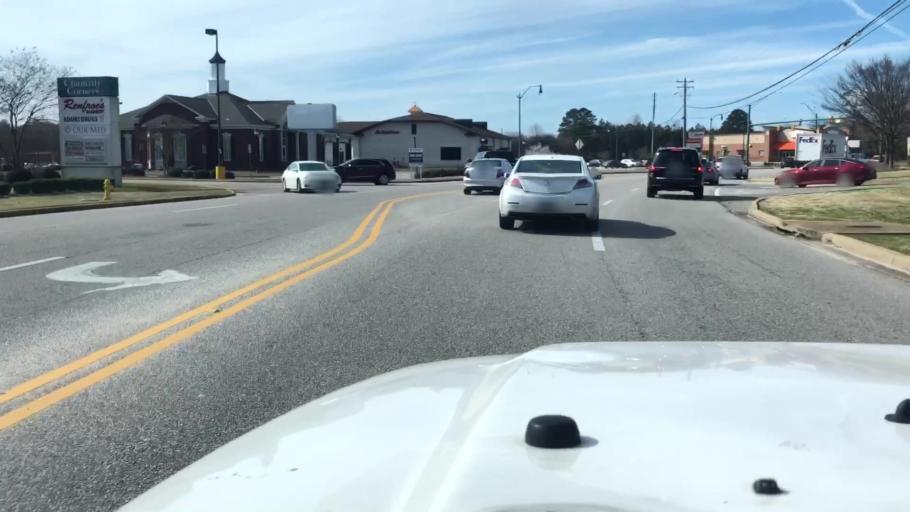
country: US
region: Alabama
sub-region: Montgomery County
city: Pike Road
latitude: 32.3623
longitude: -86.1371
